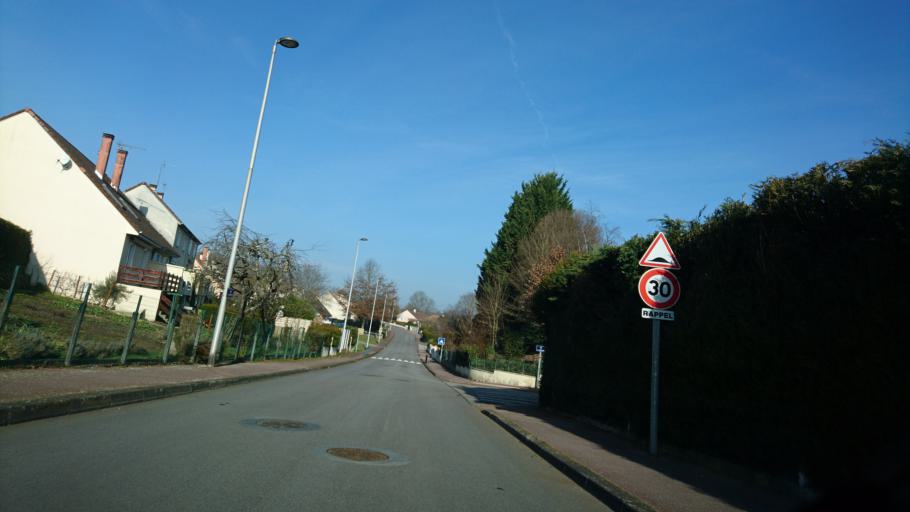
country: FR
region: Limousin
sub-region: Departement de la Haute-Vienne
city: Rilhac-Rancon
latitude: 45.8797
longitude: 1.3032
